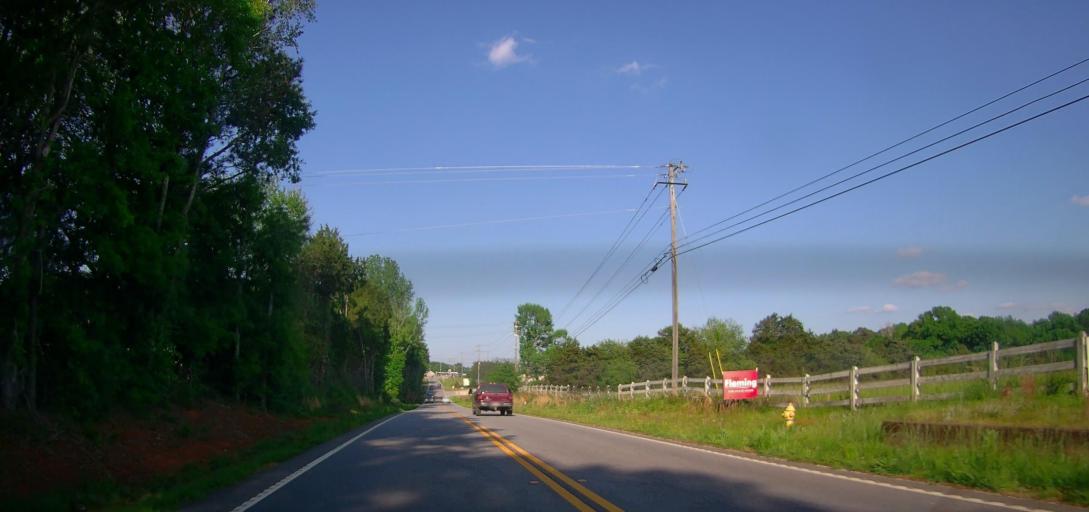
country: US
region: Georgia
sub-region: Walton County
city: Social Circle
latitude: 33.5979
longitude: -83.7577
